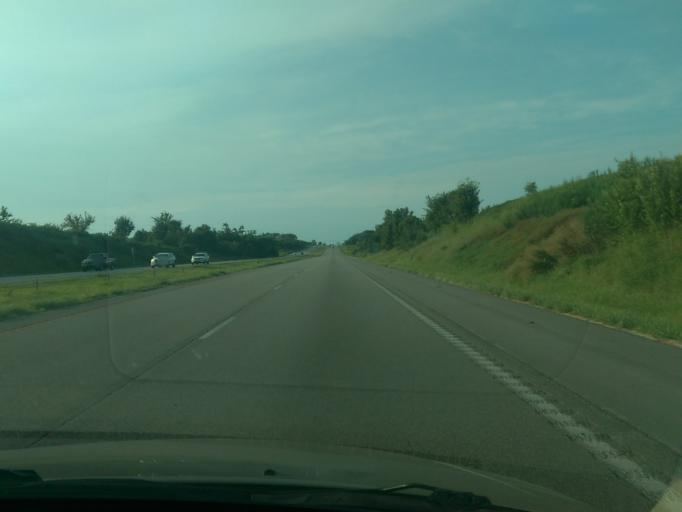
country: US
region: Missouri
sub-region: Platte County
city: Platte City
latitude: 39.4195
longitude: -94.7896
